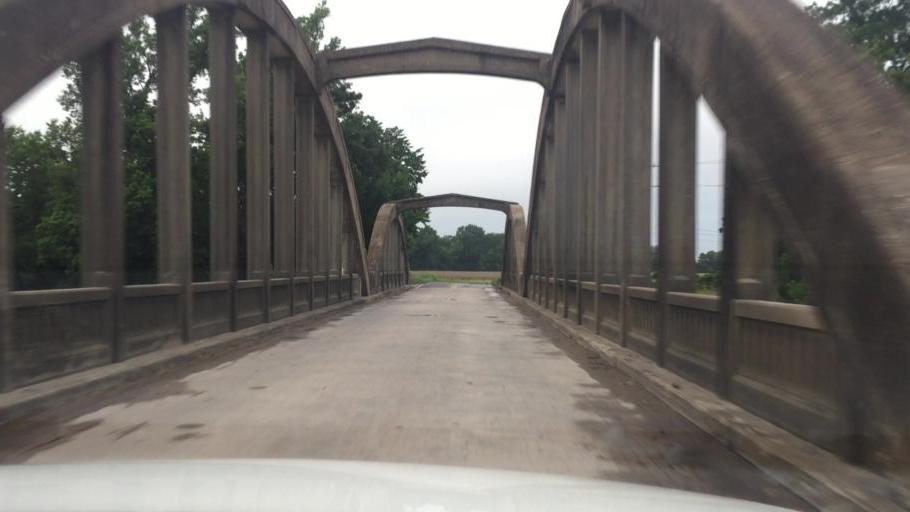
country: US
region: Kansas
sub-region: Montgomery County
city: Coffeyville
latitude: 37.0333
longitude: -95.5801
